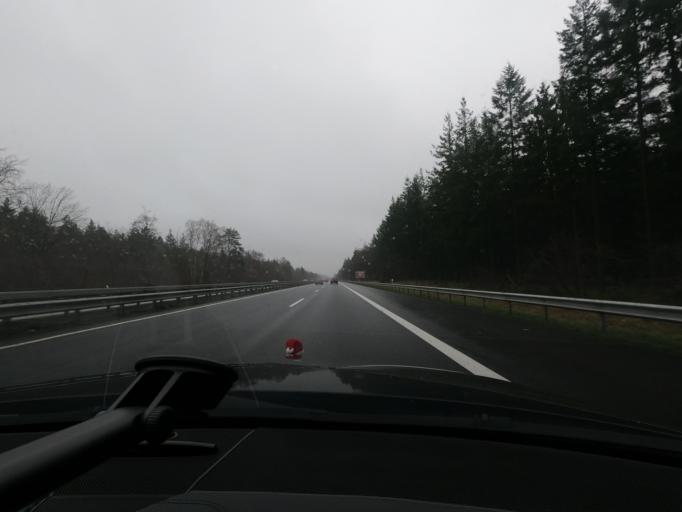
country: DE
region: Schleswig-Holstein
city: Gross Vollstedt
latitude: 54.2312
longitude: 9.8345
